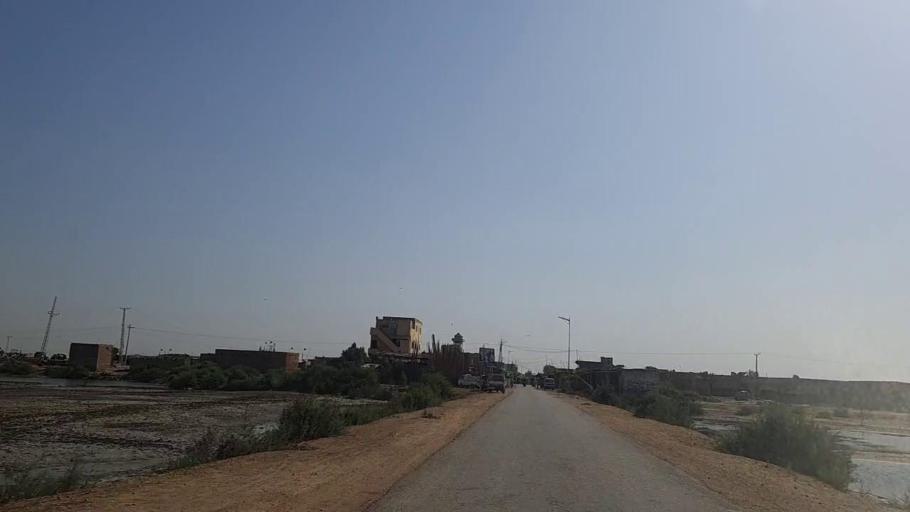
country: PK
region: Sindh
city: Mirpur Batoro
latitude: 24.6195
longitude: 68.2952
